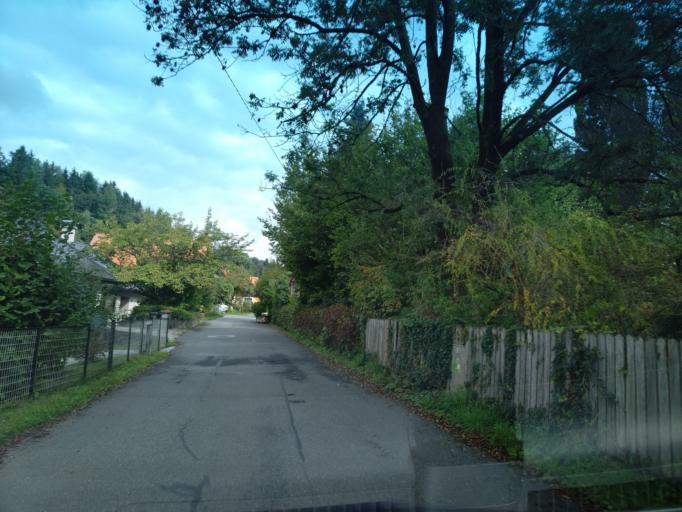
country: AT
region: Styria
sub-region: Politischer Bezirk Deutschlandsberg
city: Deutschlandsberg
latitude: 46.8225
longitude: 15.2131
